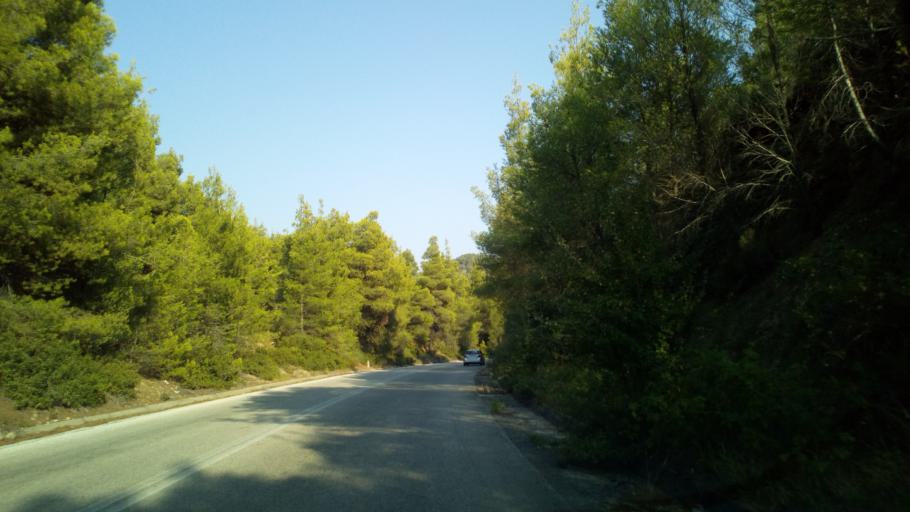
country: GR
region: Central Macedonia
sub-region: Nomos Chalkidikis
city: Neos Marmaras
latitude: 40.1796
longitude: 23.8263
